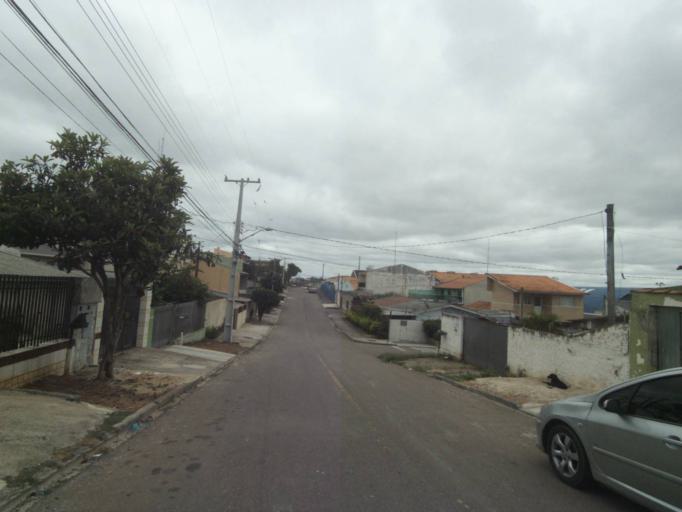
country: BR
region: Parana
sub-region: Sao Jose Dos Pinhais
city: Sao Jose dos Pinhais
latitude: -25.5462
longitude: -49.2710
